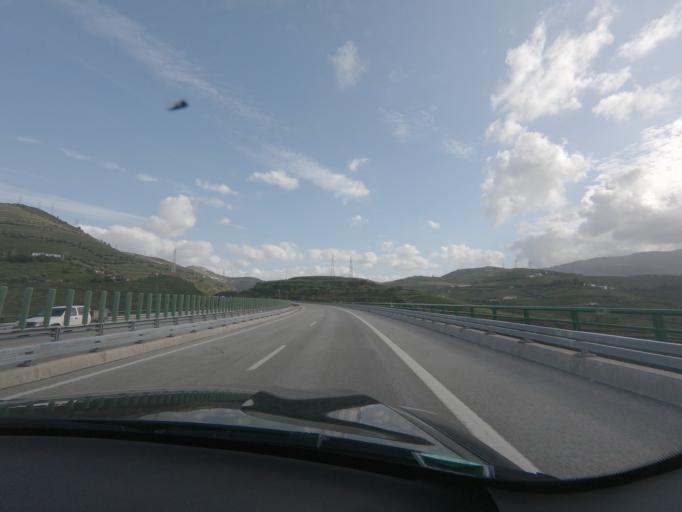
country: PT
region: Vila Real
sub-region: Peso da Regua
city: Peso da Regua
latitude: 41.1538
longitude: -7.7772
